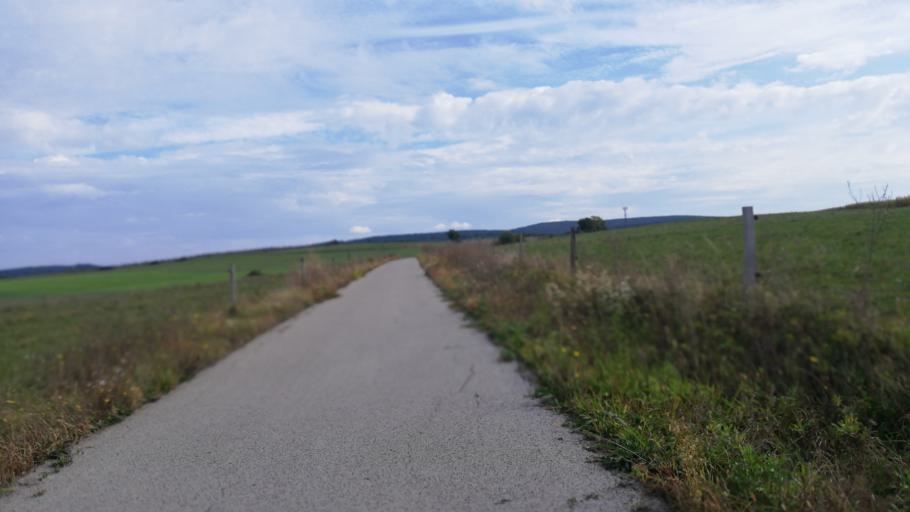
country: CZ
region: South Moravian
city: Sudomerice
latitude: 48.8429
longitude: 17.2789
